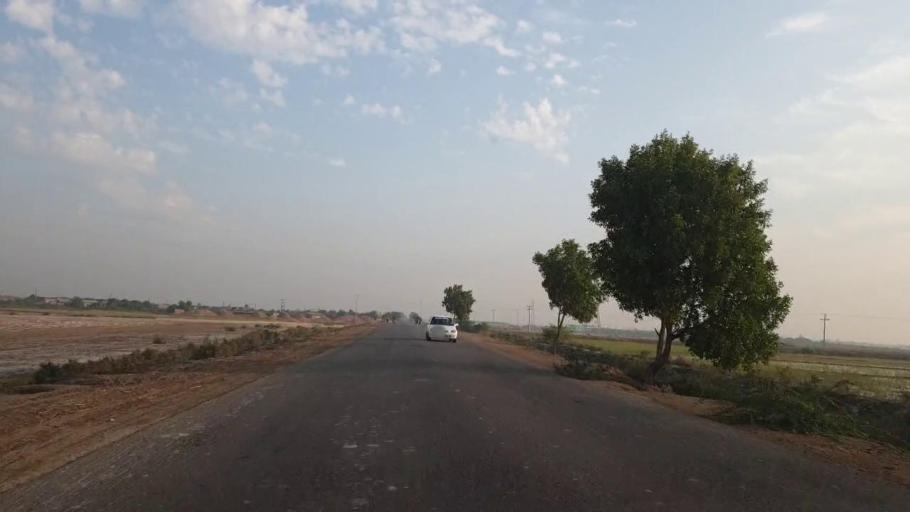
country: PK
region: Sindh
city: Badin
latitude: 24.6859
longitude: 68.9133
